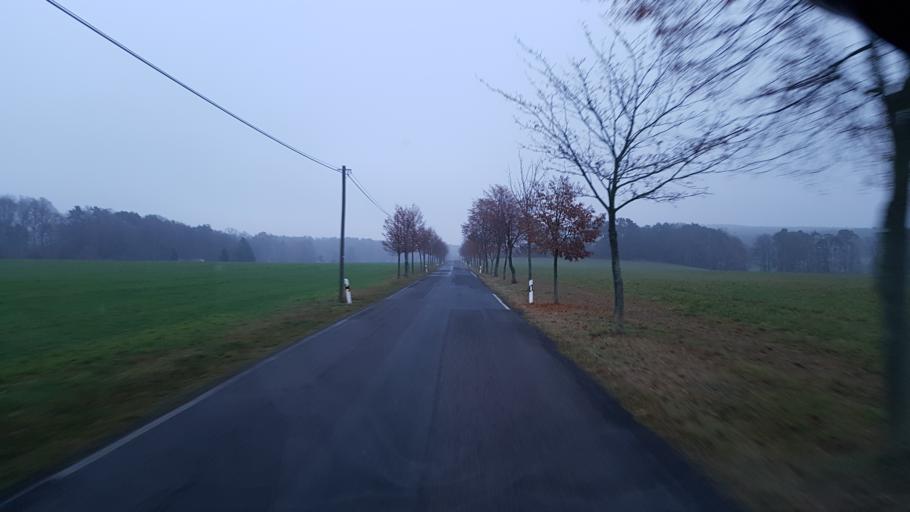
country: DE
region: Brandenburg
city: Bronkow
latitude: 51.6872
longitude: 13.9514
